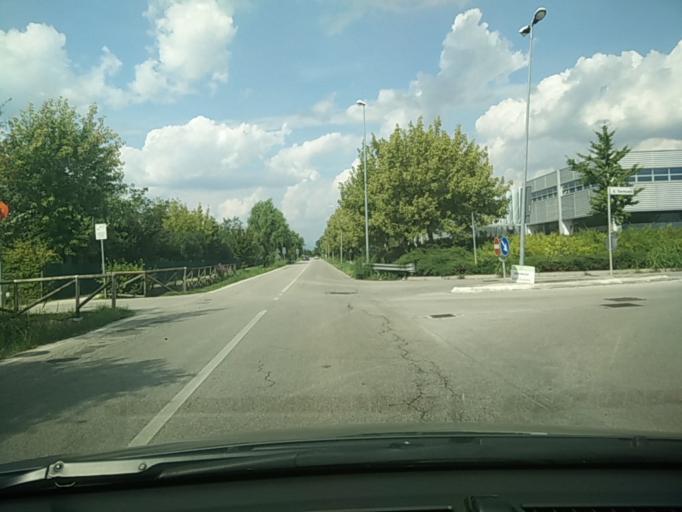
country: IT
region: Veneto
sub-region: Provincia di Treviso
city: Lancenigo-Villorba
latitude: 45.7196
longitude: 12.2415
